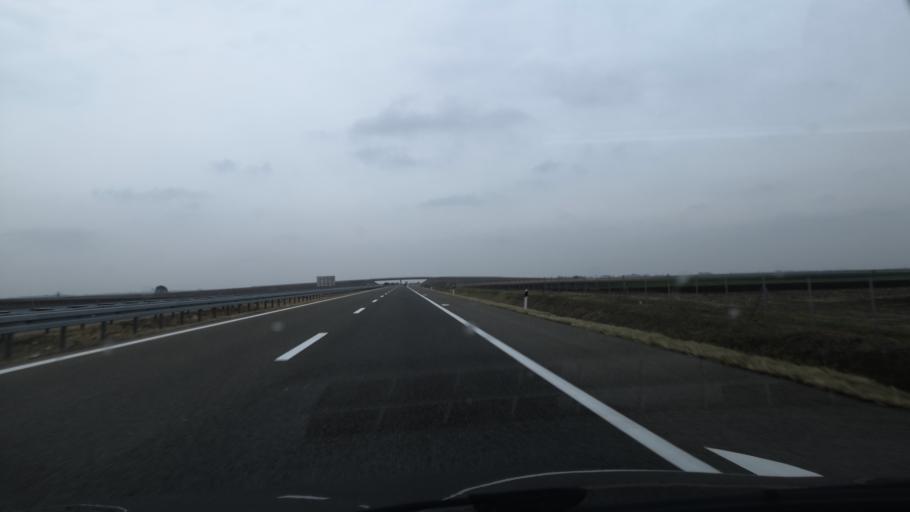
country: RS
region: Autonomna Pokrajina Vojvodina
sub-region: Severnobacki Okrug
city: Backa Topola
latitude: 45.8884
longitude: 19.6994
